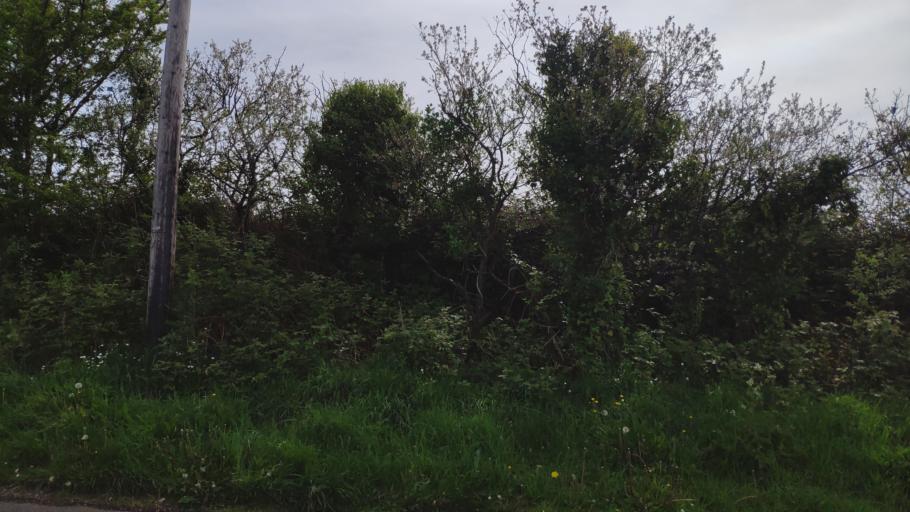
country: IE
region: Munster
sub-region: County Cork
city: Blarney
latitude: 51.9678
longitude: -8.5139
